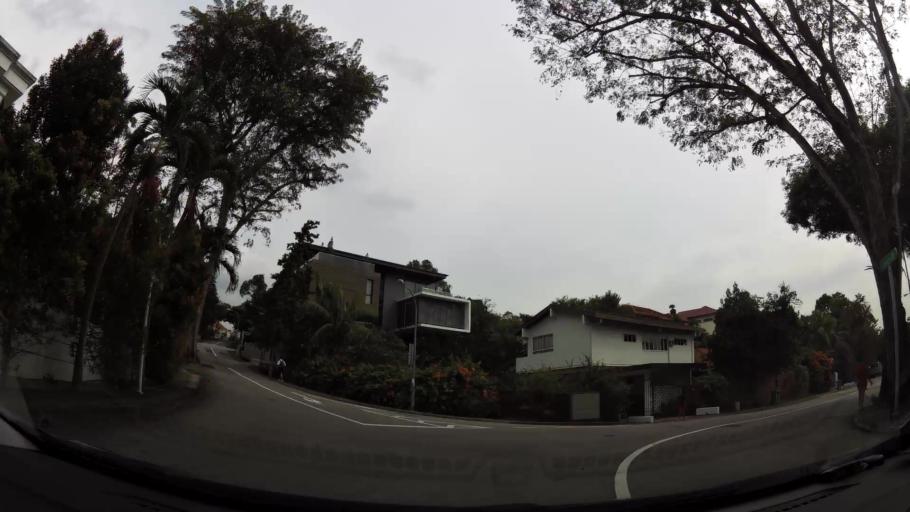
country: SG
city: Singapore
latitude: 1.3334
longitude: 103.8022
